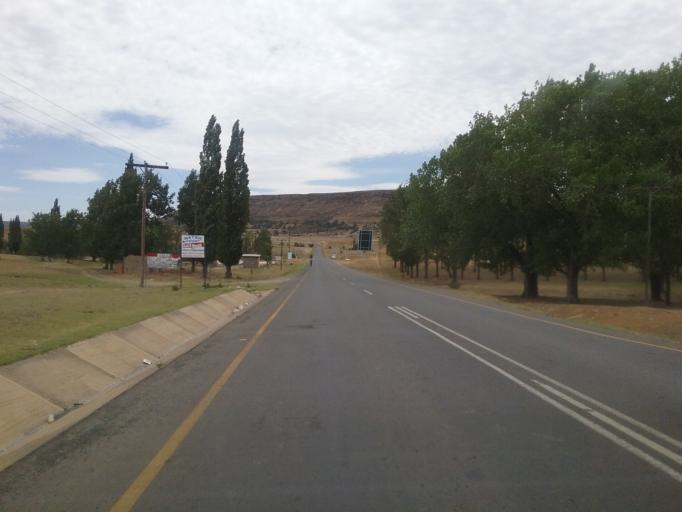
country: LS
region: Maseru
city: Nako
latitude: -29.6210
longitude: 27.4969
